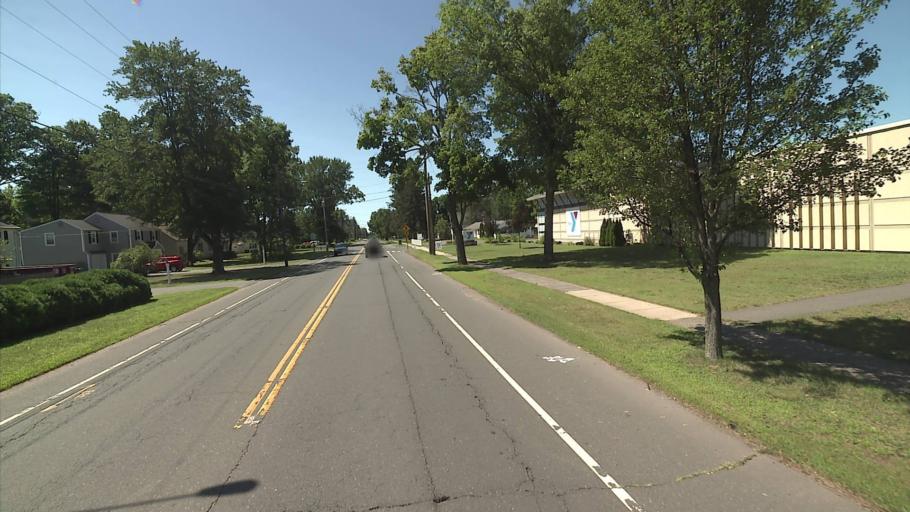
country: US
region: Connecticut
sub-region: Hartford County
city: Plainville
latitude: 41.6821
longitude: -72.8548
